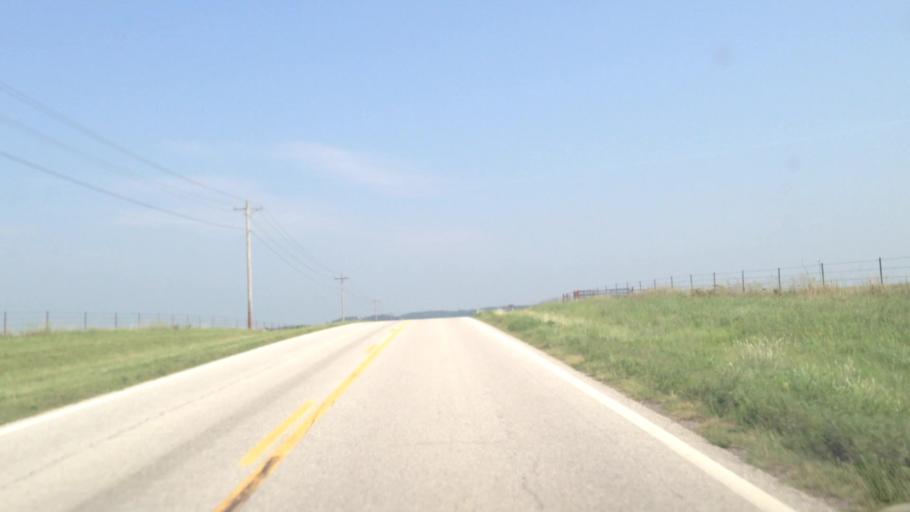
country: US
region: Oklahoma
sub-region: Craig County
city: Vinita
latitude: 36.7395
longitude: -95.1435
